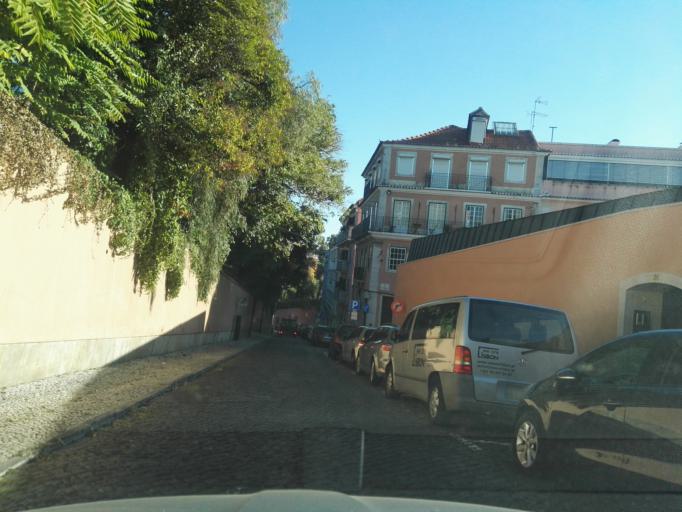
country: PT
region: Setubal
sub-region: Almada
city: Cacilhas
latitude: 38.7064
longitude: -9.1633
